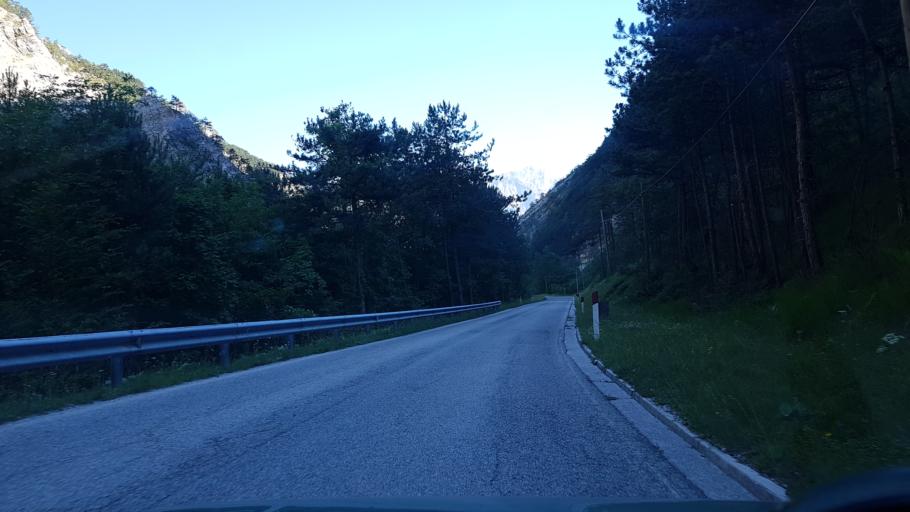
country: IT
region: Friuli Venezia Giulia
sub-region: Provincia di Udine
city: Moggio Udinese
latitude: 46.4421
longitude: 13.1945
